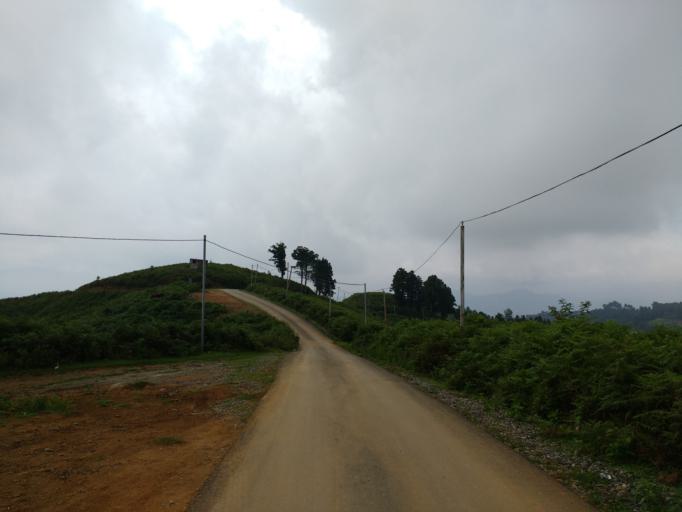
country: GE
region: Ajaria
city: Khelvachauri
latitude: 41.5641
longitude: 41.5842
